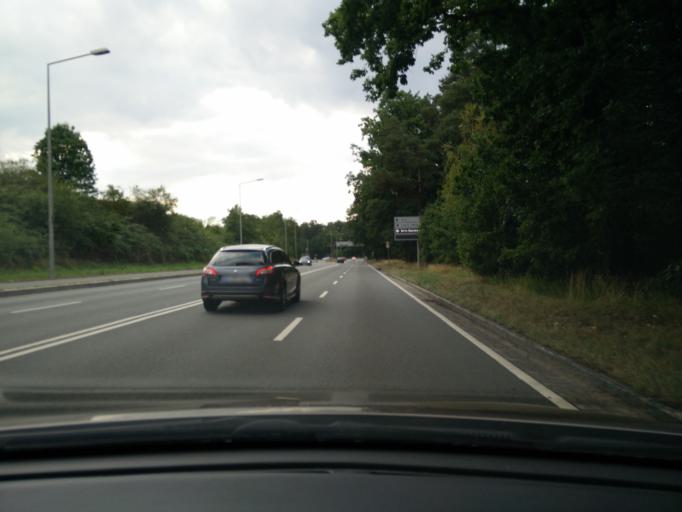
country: DE
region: Bavaria
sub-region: Regierungsbezirk Mittelfranken
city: Nuernberg
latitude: 49.4194
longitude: 11.1342
